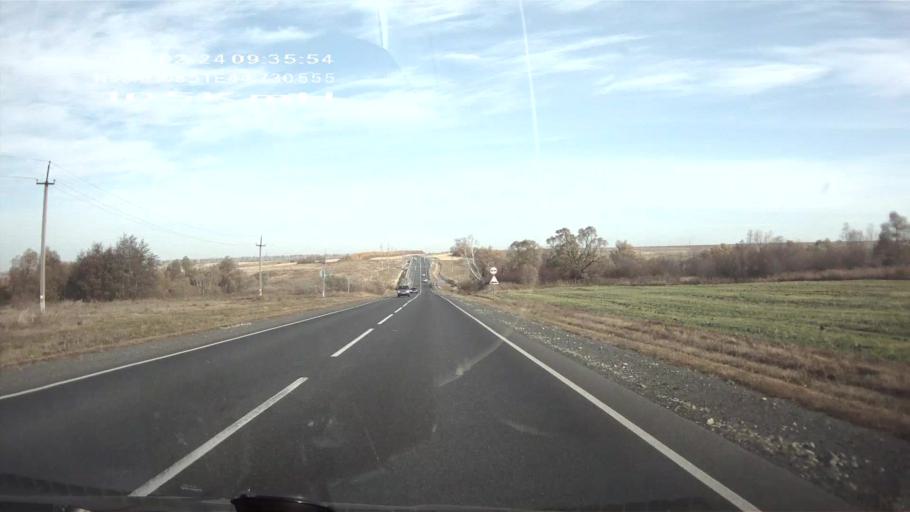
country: RU
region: Penza
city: Mokshan
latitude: 53.6110
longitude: 44.7306
